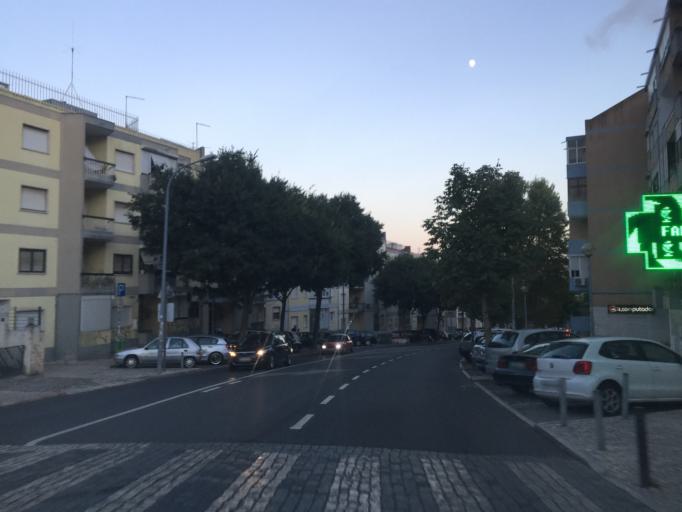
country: PT
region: Lisbon
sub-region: Odivelas
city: Odivelas
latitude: 38.7937
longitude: -9.1781
